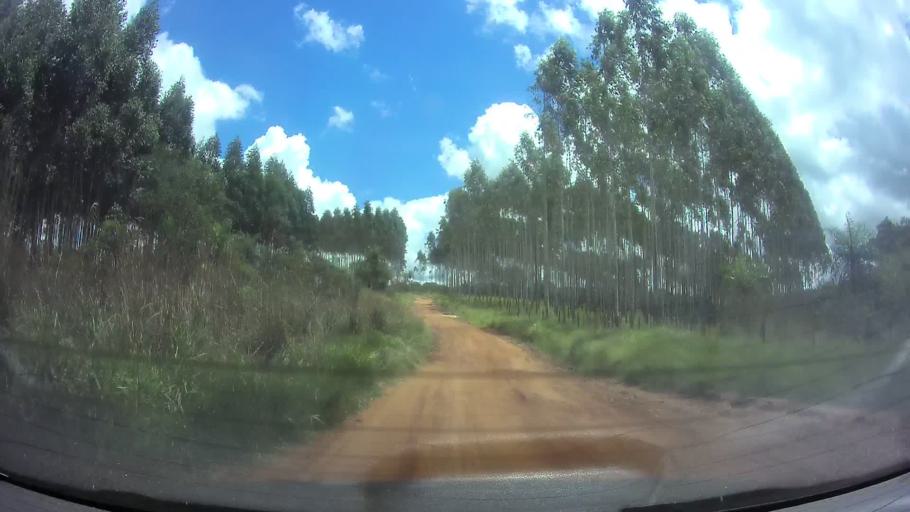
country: PY
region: Paraguari
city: La Colmena
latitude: -25.9660
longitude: -56.7477
